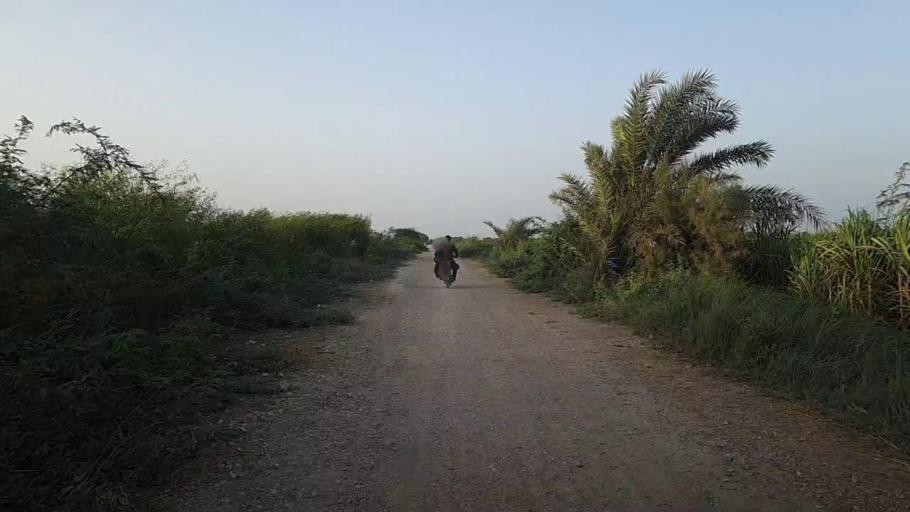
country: PK
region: Sindh
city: Kario
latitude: 24.7142
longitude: 68.4621
